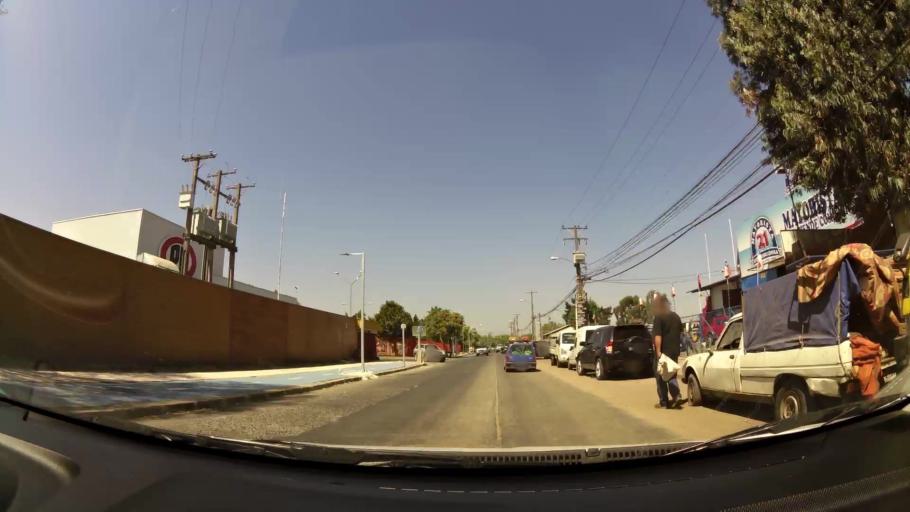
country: CL
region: Maule
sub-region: Provincia de Talca
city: Talca
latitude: -35.4221
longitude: -71.6366
